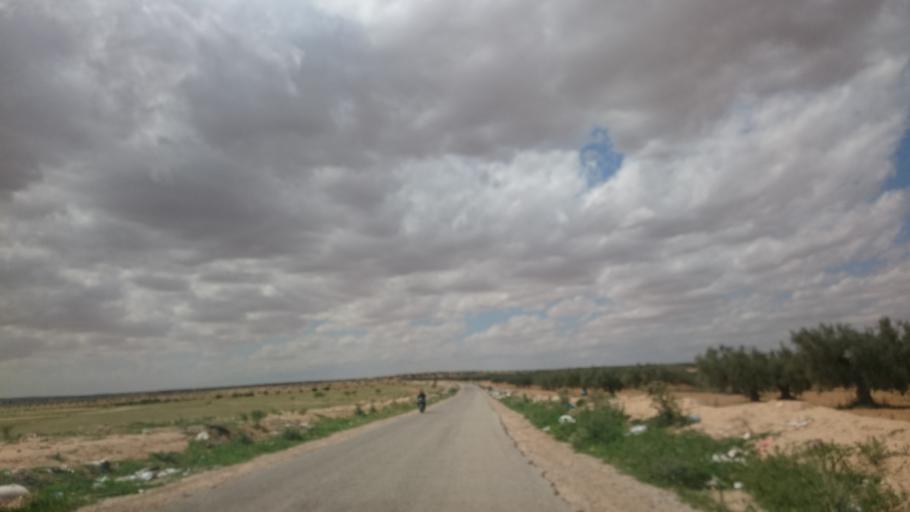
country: TN
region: Safaqis
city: Sfax
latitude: 34.7477
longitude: 10.5103
